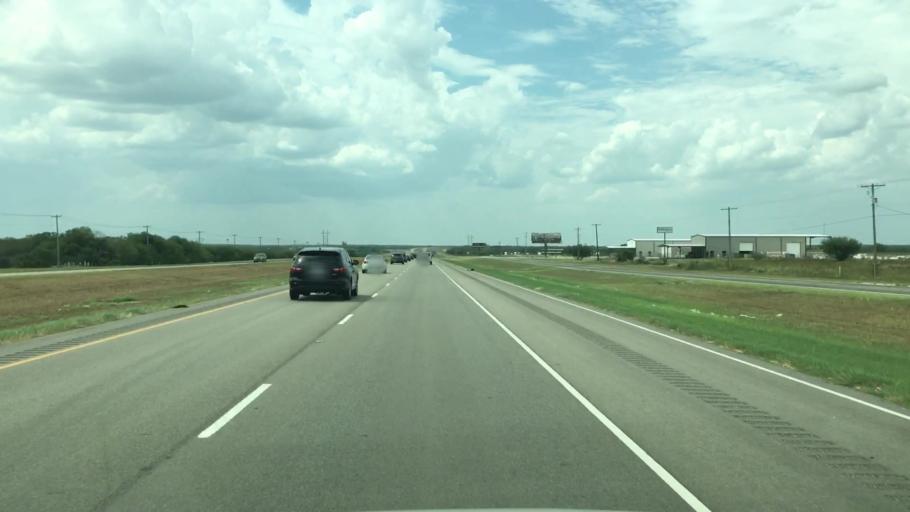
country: US
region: Texas
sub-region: Live Oak County
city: Three Rivers
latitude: 28.5077
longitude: -98.1646
